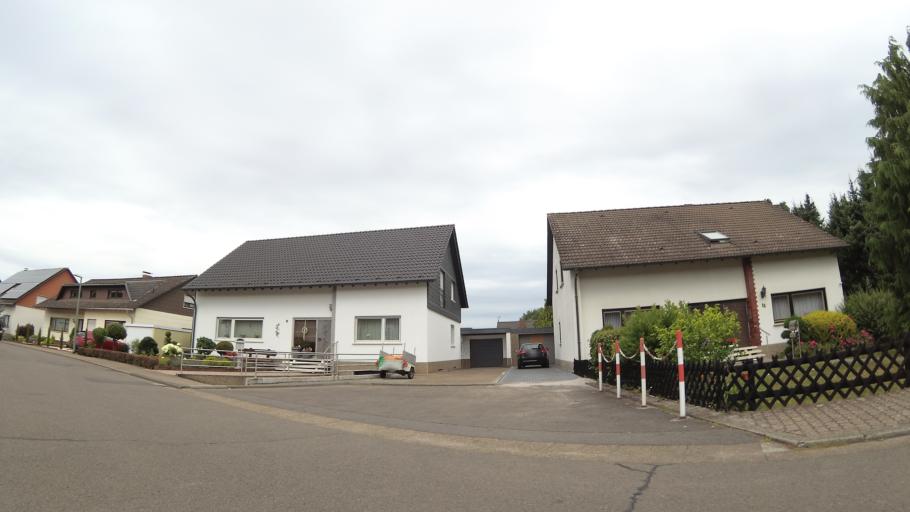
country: DE
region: Saarland
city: Schwalbach
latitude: 49.3118
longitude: 6.8107
